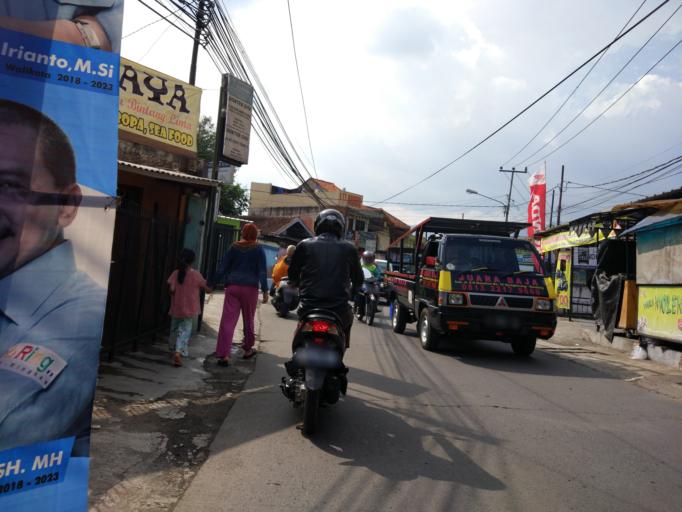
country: ID
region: West Java
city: Cileunyi
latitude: -6.9081
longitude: 107.6909
